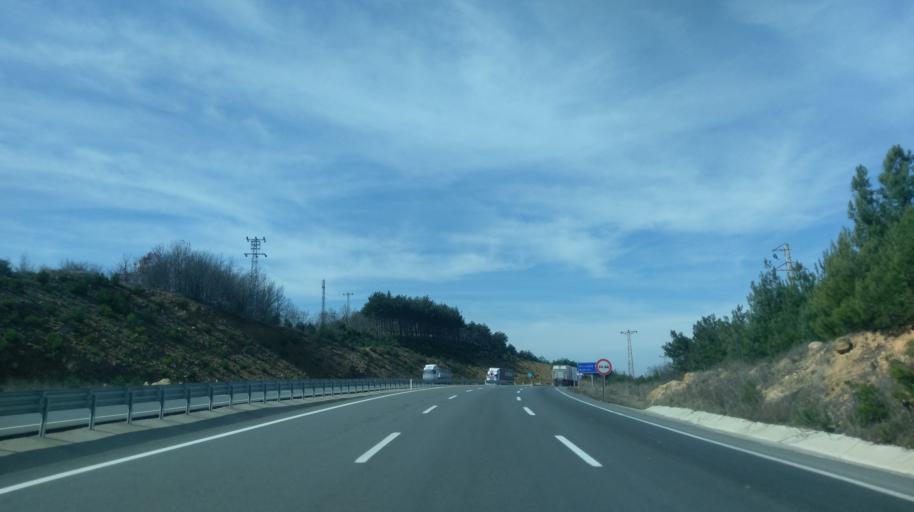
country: TR
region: Canakkale
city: Evrese
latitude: 40.7082
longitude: 26.7718
